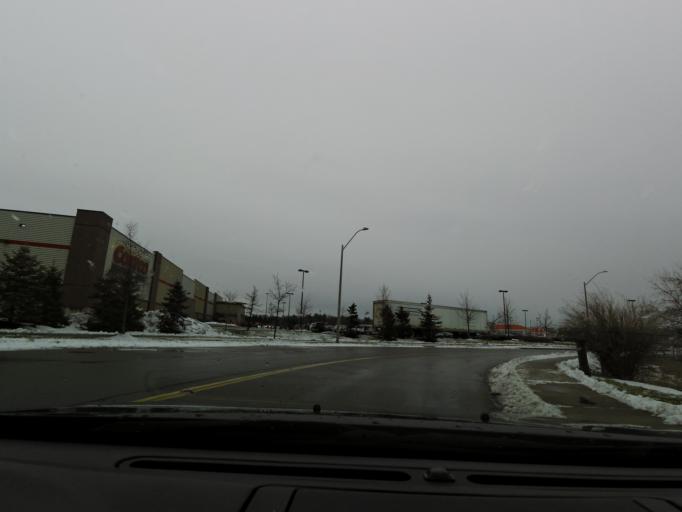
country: CA
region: Ontario
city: Ancaster
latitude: 43.2287
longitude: -79.9481
